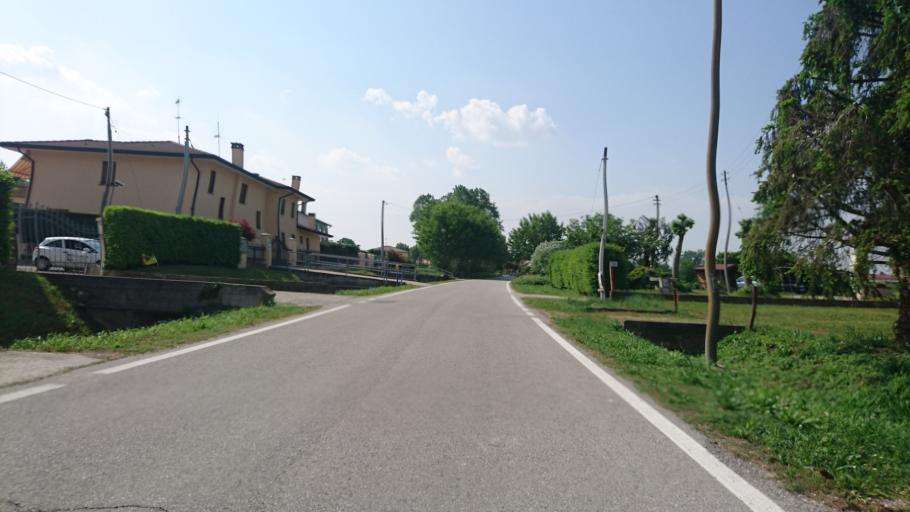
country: IT
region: Veneto
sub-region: Provincia di Venezia
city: Tombelle
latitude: 45.3856
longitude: 11.9805
